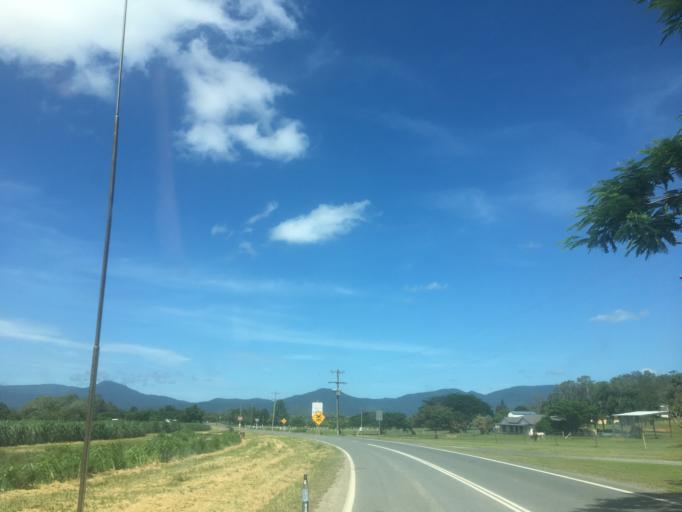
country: AU
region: Queensland
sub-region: Cairns
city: Woree
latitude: -17.0673
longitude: 145.7512
